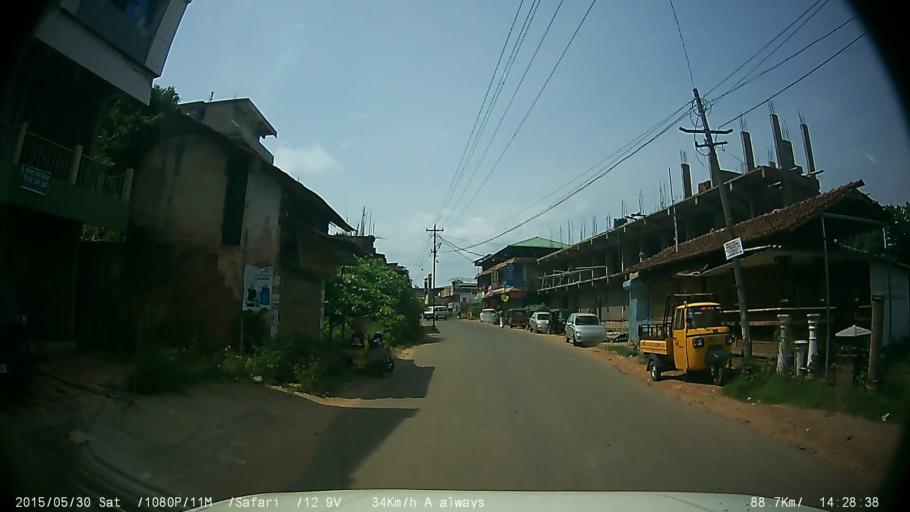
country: IN
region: Kerala
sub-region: Wayanad
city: Panamaram
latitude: 11.8002
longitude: 76.0027
